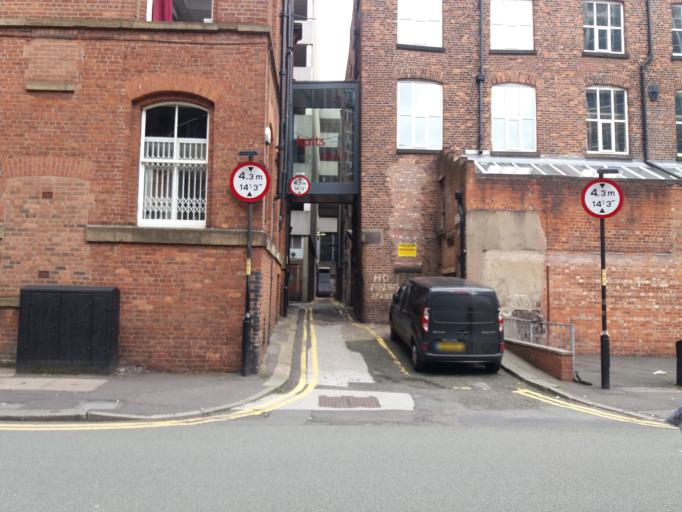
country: GB
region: England
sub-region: Manchester
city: Manchester
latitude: 53.4820
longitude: -2.2501
